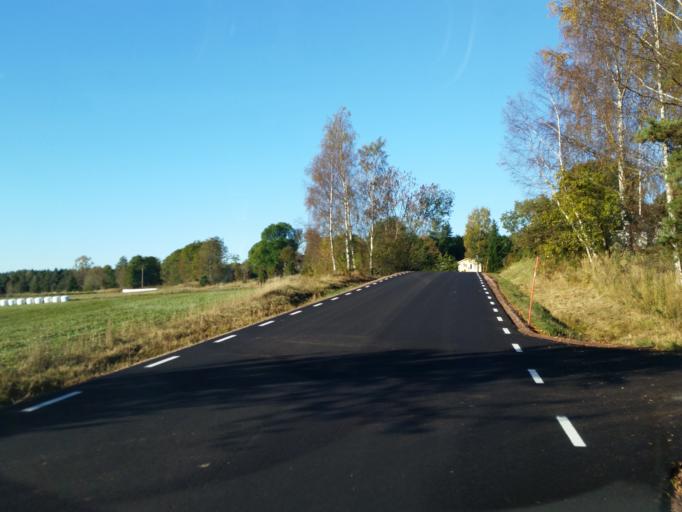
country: AX
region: Alands landsbygd
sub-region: Sund
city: Sund
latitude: 60.2218
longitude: 20.0966
